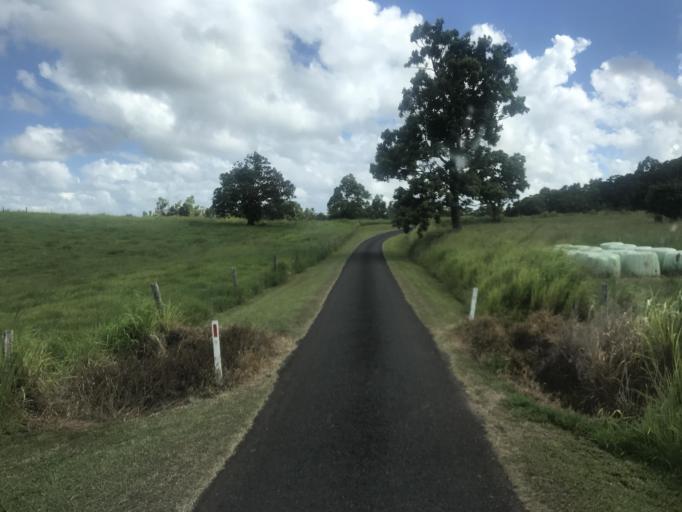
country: AU
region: Queensland
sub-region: Tablelands
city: Ravenshoe
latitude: -17.5561
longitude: 145.6904
